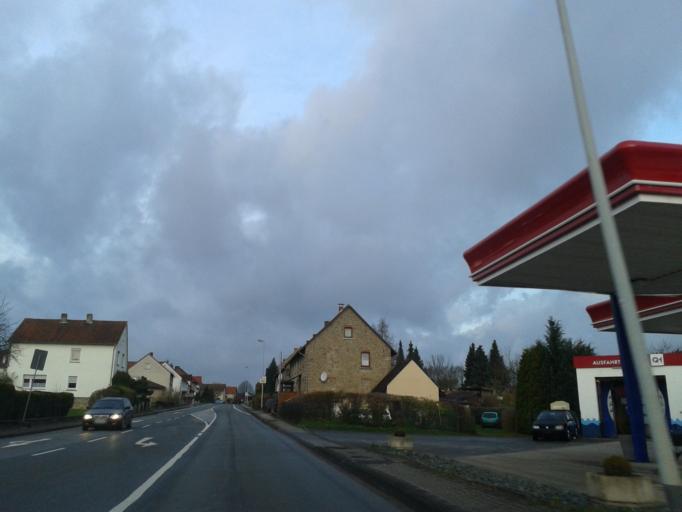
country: DE
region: North Rhine-Westphalia
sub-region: Regierungsbezirk Detmold
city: Blomberg
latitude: 51.9480
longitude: 9.0570
